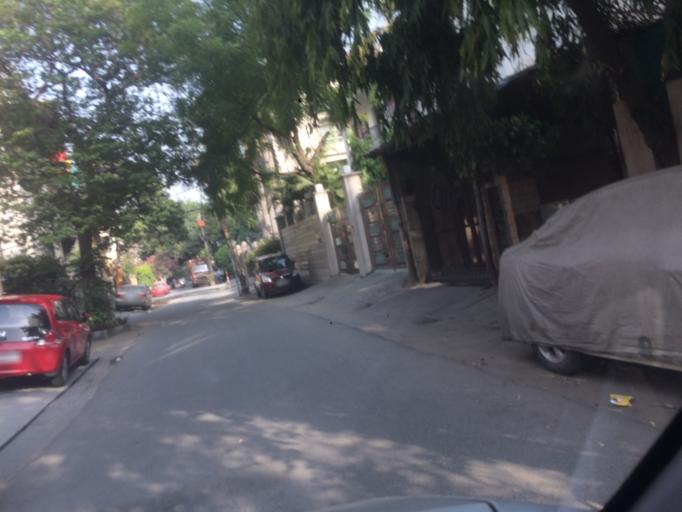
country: IN
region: NCT
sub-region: New Delhi
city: New Delhi
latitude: 28.5580
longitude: 77.2345
